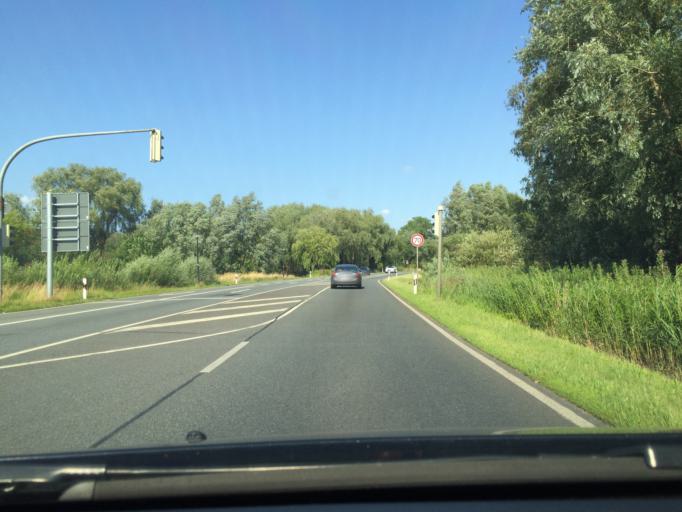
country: DE
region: Mecklenburg-Vorpommern
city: Ribnitz-Damgarten
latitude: 54.2493
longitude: 12.4717
